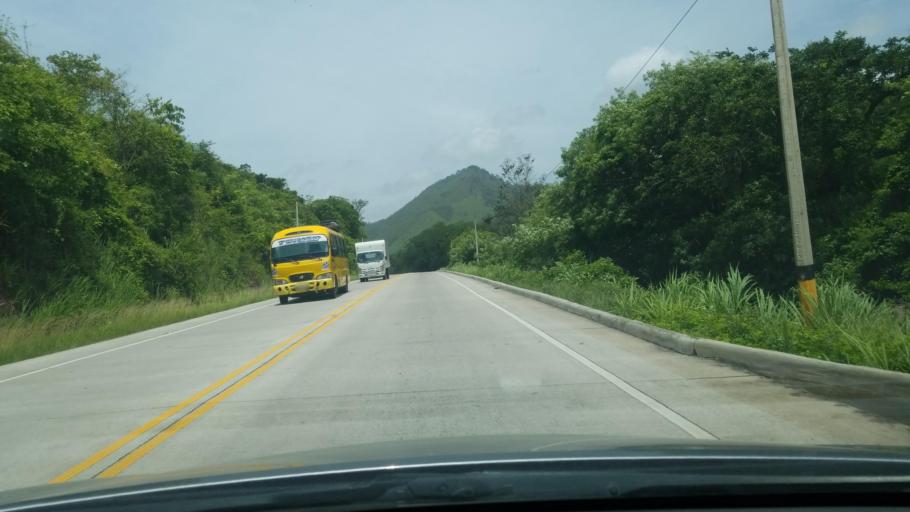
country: HN
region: Copan
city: Quezailica
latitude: 14.8891
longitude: -88.7655
